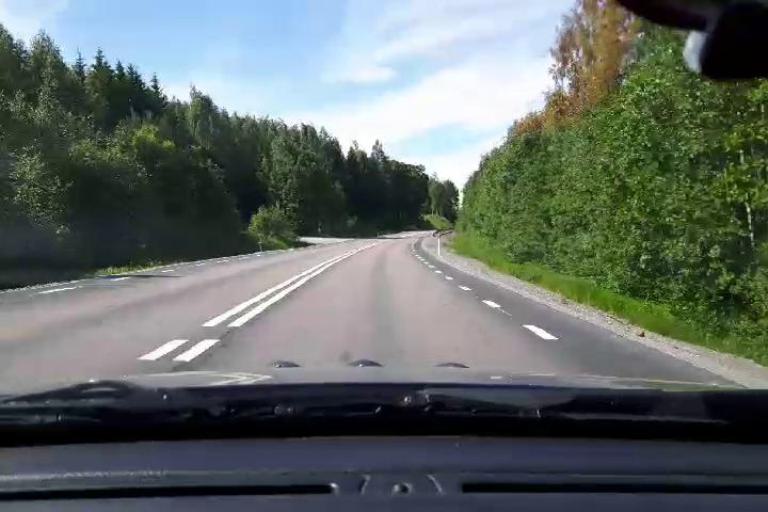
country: SE
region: Gaevleborg
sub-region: Bollnas Kommun
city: Kilafors
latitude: 61.1878
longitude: 16.7750
